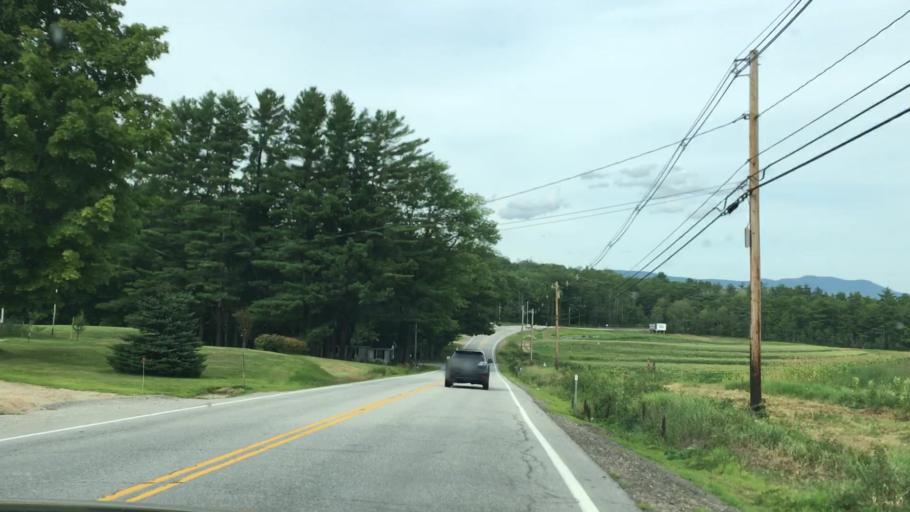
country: US
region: New Hampshire
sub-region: Carroll County
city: Center Harbor
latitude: 43.6795
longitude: -71.4717
